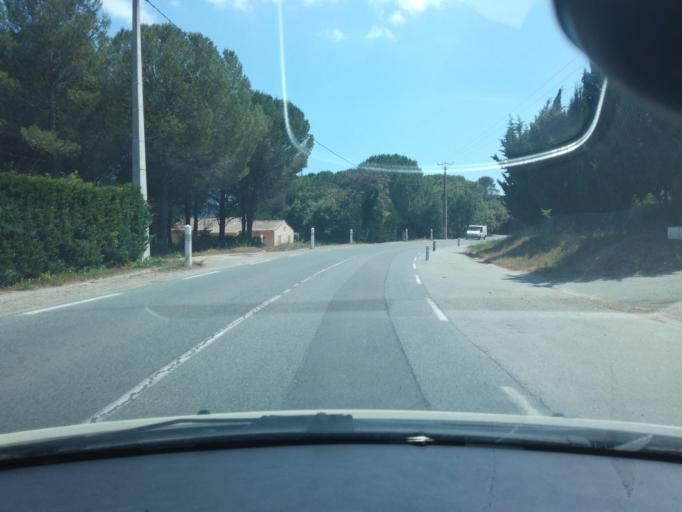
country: FR
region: Provence-Alpes-Cote d'Azur
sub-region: Departement du Var
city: Le Muy
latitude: 43.4862
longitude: 6.5674
